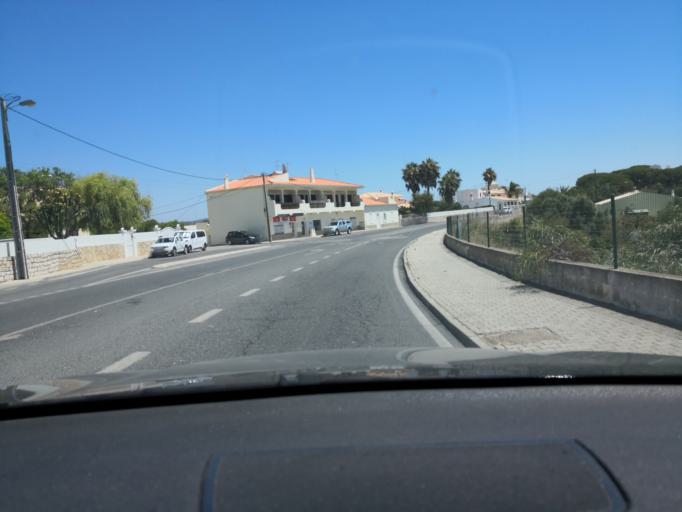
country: PT
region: Faro
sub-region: Albufeira
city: Ferreiras
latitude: 37.1082
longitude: -8.2100
